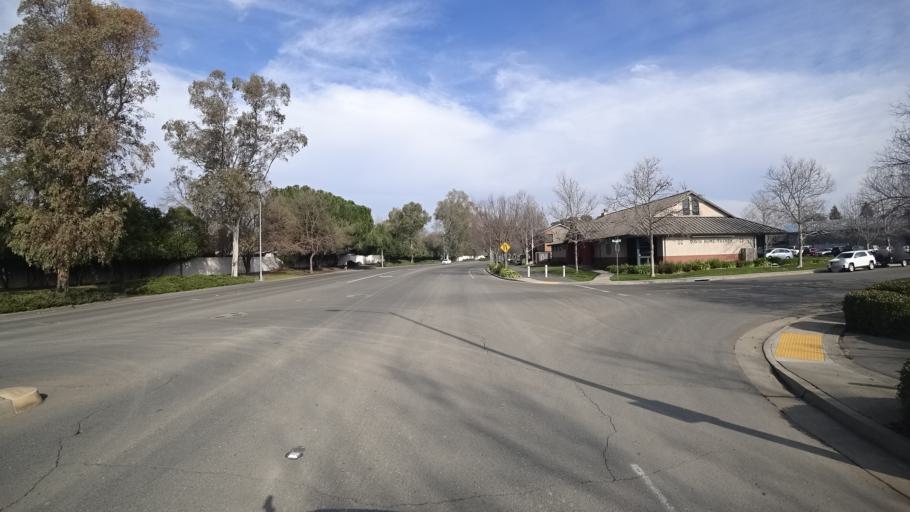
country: US
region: California
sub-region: Yolo County
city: Davis
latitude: 38.5503
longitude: -121.7232
